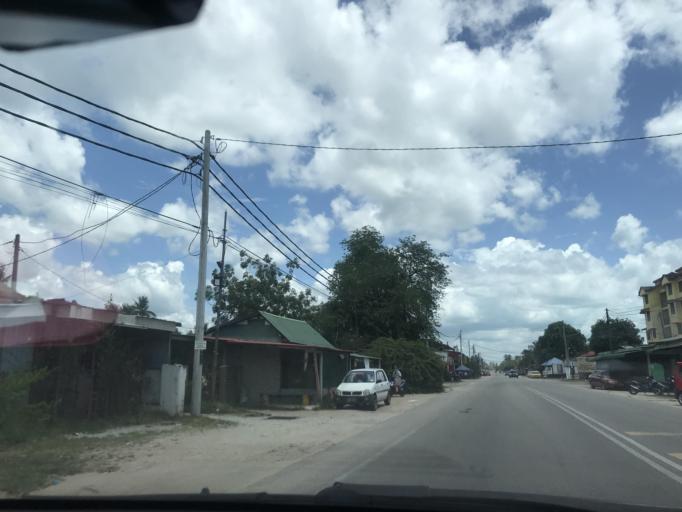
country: TH
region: Narathiwat
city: Tak Bai
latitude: 6.2247
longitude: 102.1049
